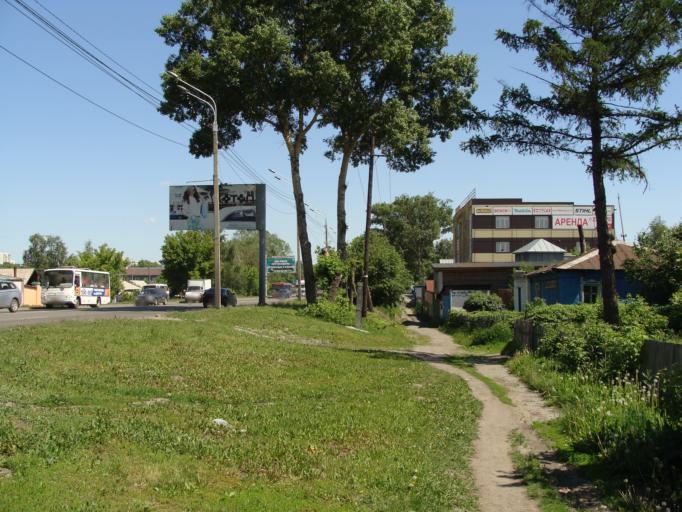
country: RU
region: Altai Krai
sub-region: Gorod Barnaulskiy
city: Barnaul
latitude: 53.3398
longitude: 83.7285
